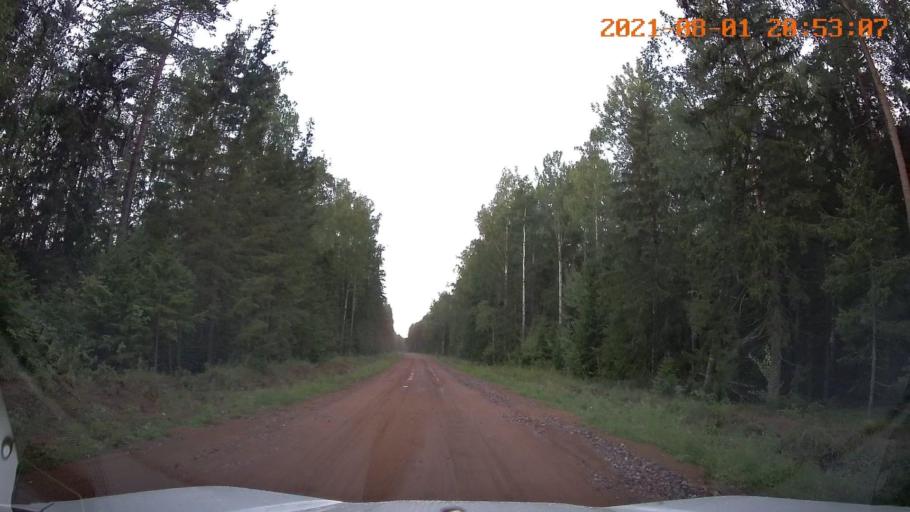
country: RU
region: Leningrad
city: Syas'stroy
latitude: 60.4466
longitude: 32.7031
